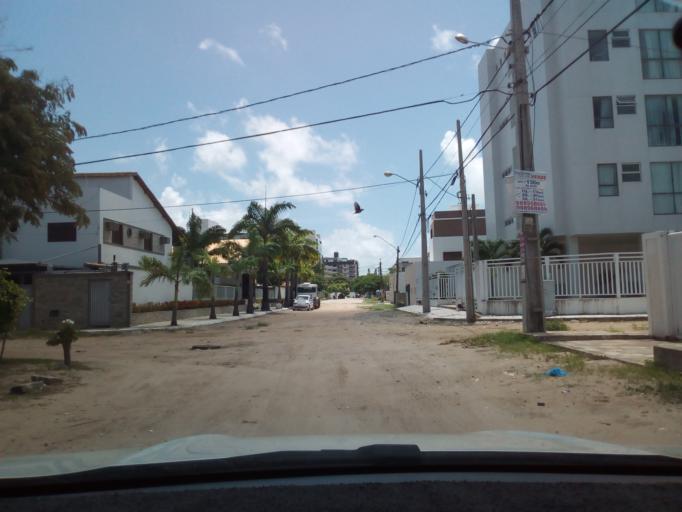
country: BR
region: Paraiba
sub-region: Cabedelo
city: Cabedelo
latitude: -6.9993
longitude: -34.8269
